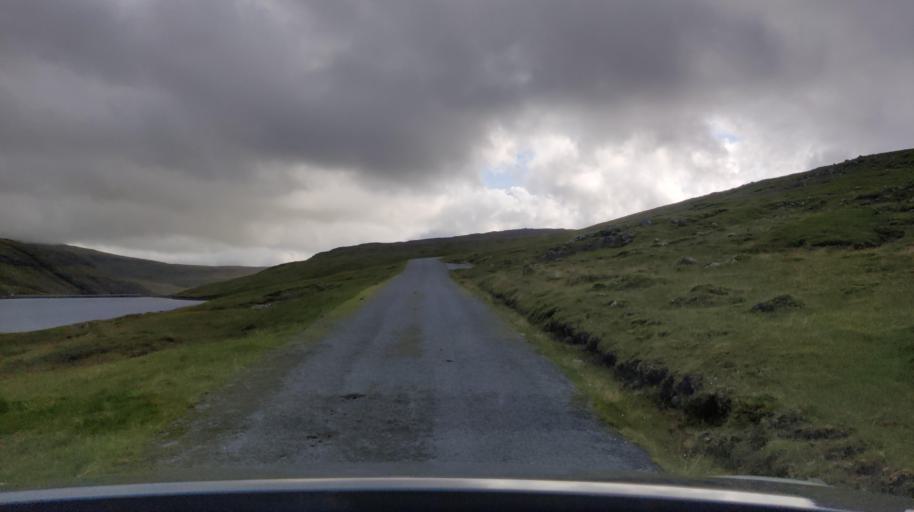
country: FO
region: Streymoy
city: Vestmanna
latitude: 62.1755
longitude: -7.1546
